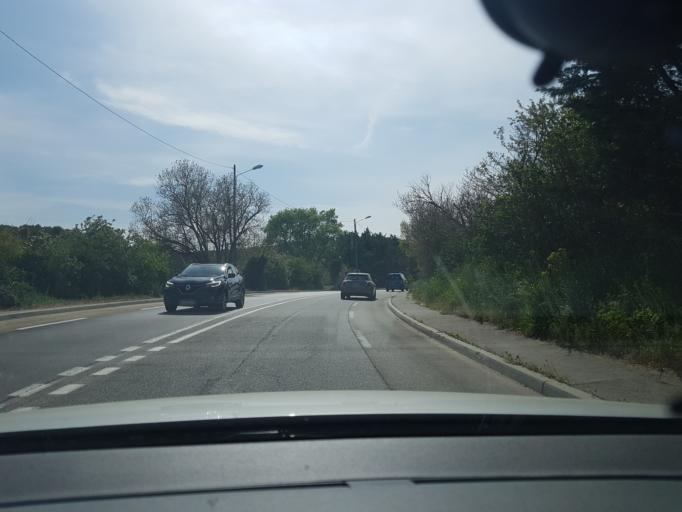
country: FR
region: Provence-Alpes-Cote d'Azur
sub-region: Departement des Bouches-du-Rhone
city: Bouc-Bel-Air
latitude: 43.4754
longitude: 5.4137
